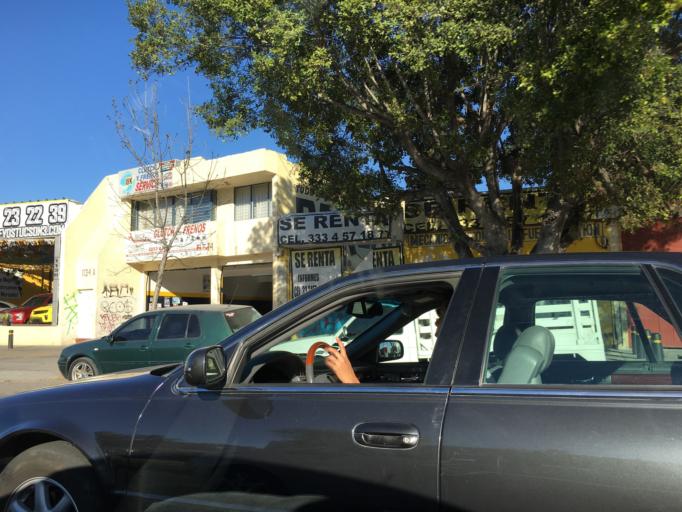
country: MX
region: Jalisco
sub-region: Zapopan
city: Zapopan
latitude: 20.6936
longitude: -103.3540
